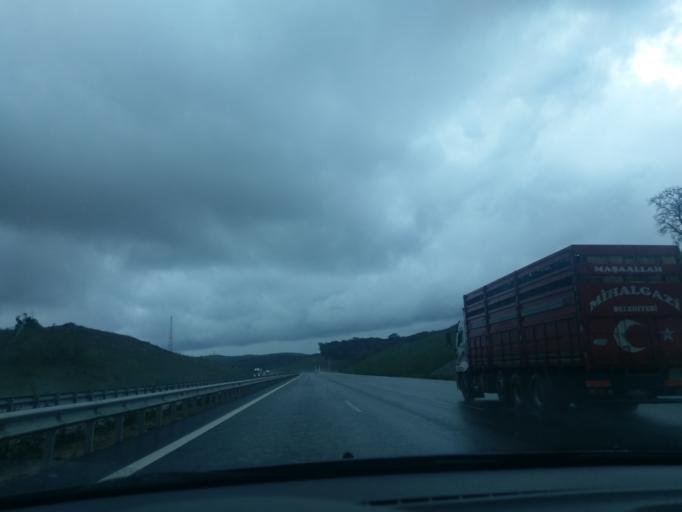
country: TR
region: Istanbul
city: Kemerburgaz
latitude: 41.2323
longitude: 28.9258
